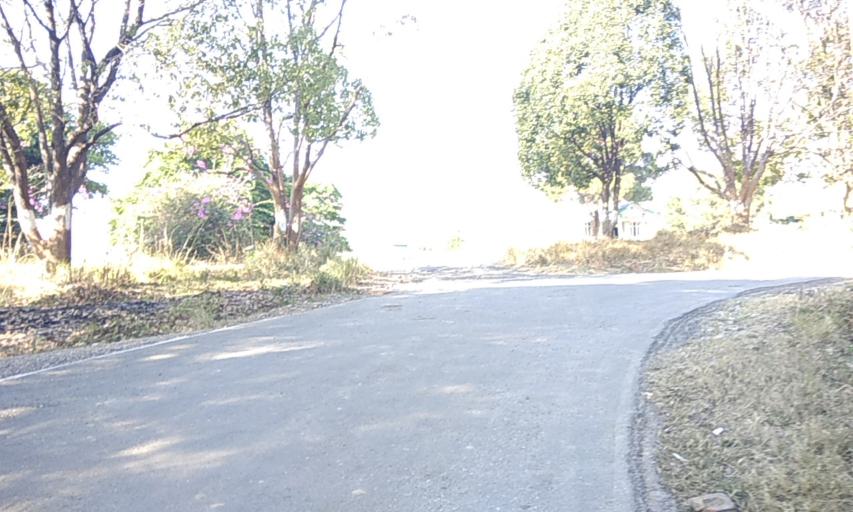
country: IN
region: Himachal Pradesh
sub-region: Kangra
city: Palampur
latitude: 32.1020
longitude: 76.5489
